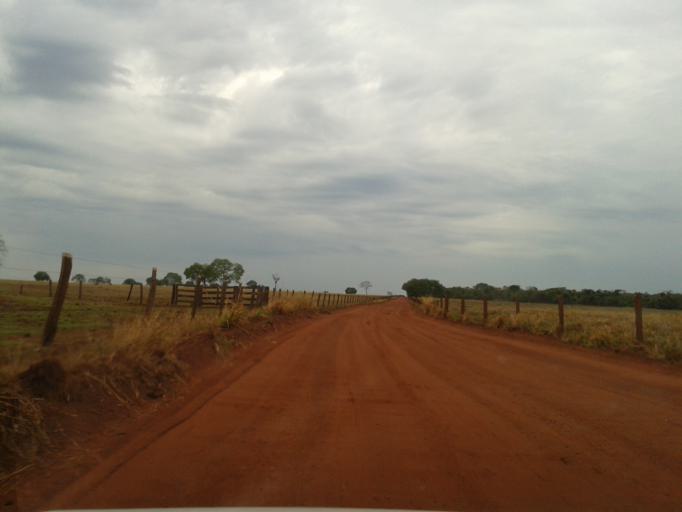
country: BR
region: Minas Gerais
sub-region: Ituiutaba
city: Ituiutaba
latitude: -18.9380
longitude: -49.7334
